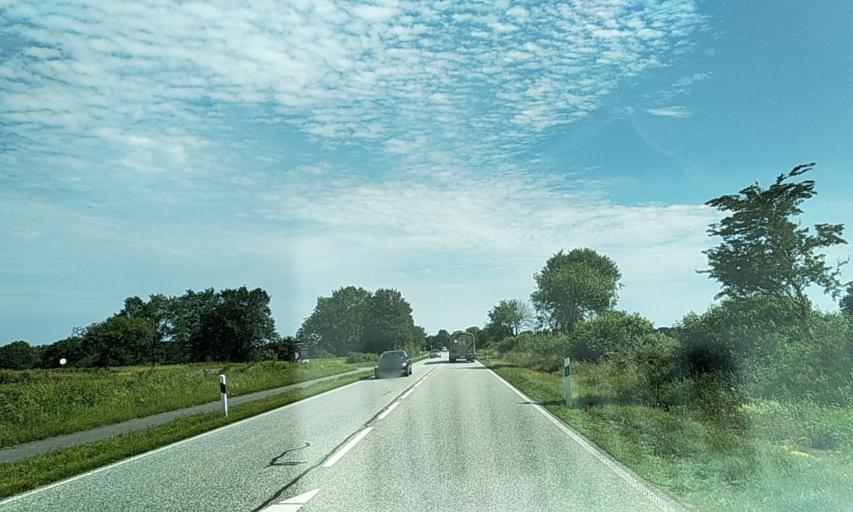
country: DE
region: Schleswig-Holstein
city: Jagel
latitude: 54.4678
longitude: 9.5420
